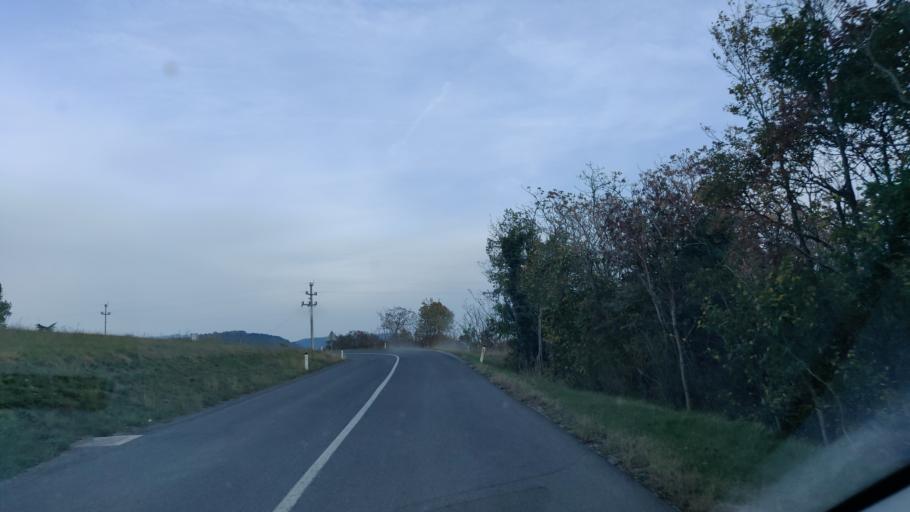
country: SI
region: Komen
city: Komen
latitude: 45.8200
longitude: 13.8367
